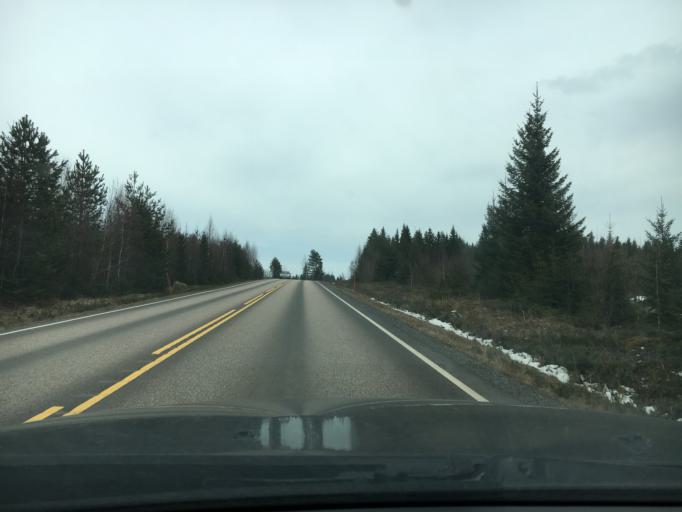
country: FI
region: Central Finland
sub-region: AEaenekoski
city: Konnevesi
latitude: 62.6973
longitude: 26.4372
